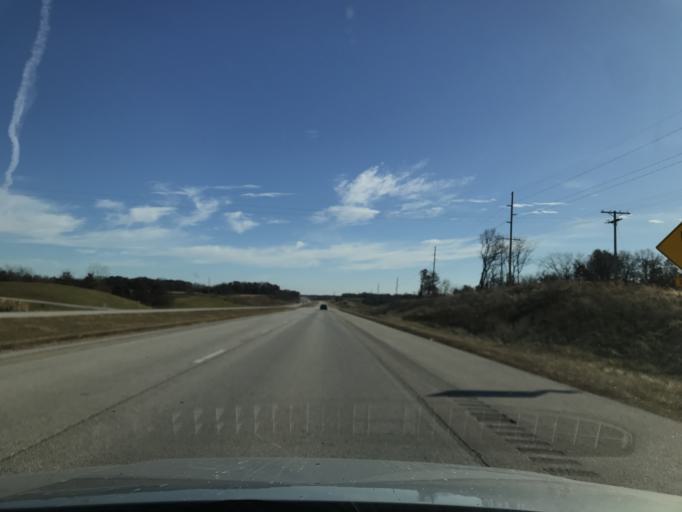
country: US
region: Illinois
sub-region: Hancock County
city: Carthage
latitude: 40.4146
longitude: -91.0379
